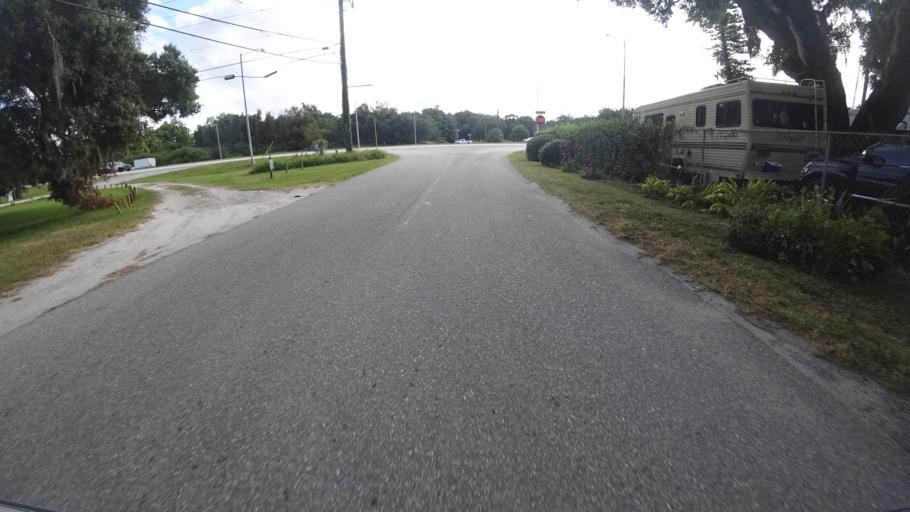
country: US
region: Florida
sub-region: Manatee County
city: Memphis
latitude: 27.5433
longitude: -82.5651
